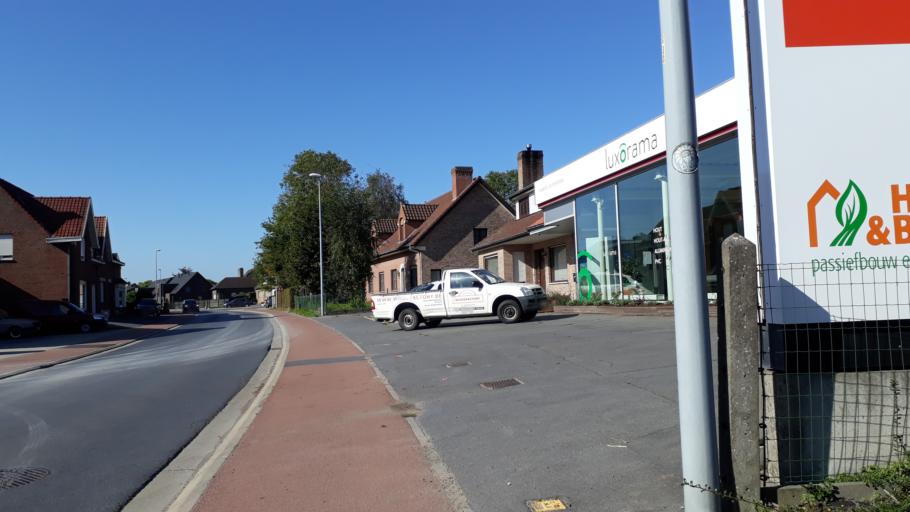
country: BE
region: Flanders
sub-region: Provincie West-Vlaanderen
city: Torhout
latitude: 51.0805
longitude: 3.1208
